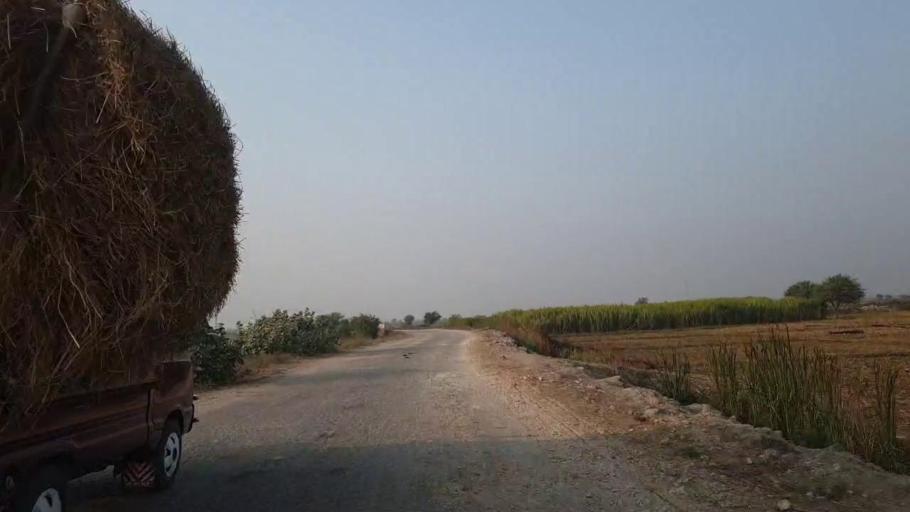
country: PK
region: Sindh
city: Tando Muhammad Khan
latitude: 25.0838
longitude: 68.4336
